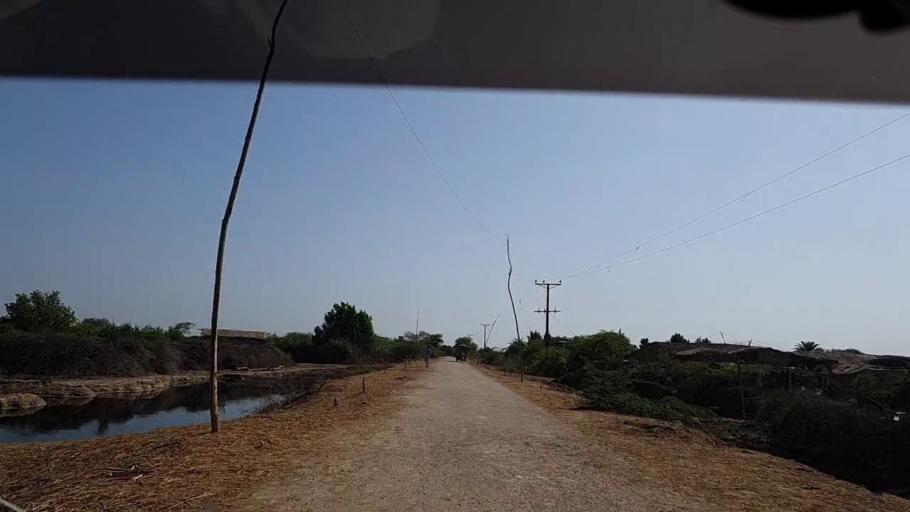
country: PK
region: Sindh
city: Badin
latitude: 24.6381
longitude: 68.7870
